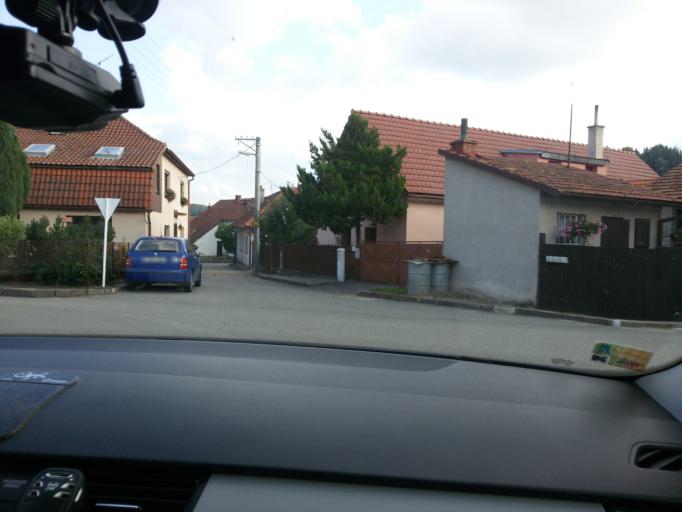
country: CZ
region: South Moravian
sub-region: Okres Brno-Venkov
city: Lomnice
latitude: 49.4623
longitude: 16.4259
